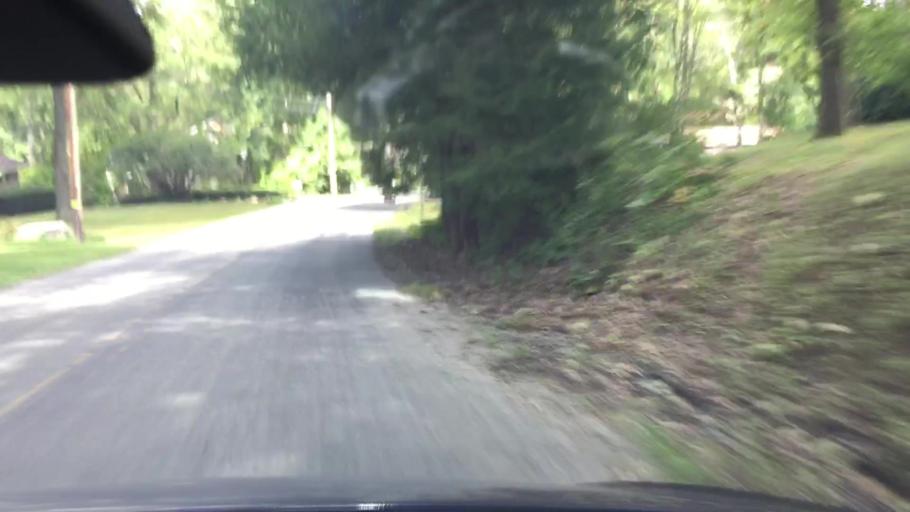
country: US
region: Pennsylvania
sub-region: Butler County
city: Meadowood
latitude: 40.7966
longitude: -79.8671
